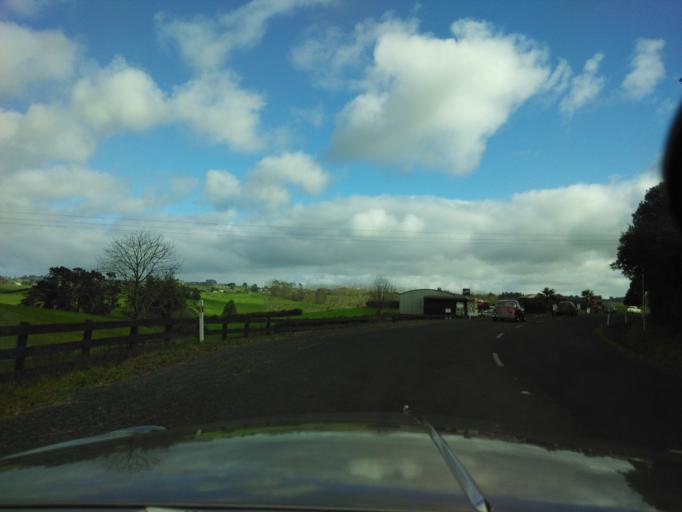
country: NZ
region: Auckland
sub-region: Auckland
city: Red Hill
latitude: -37.0824
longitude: 175.0740
